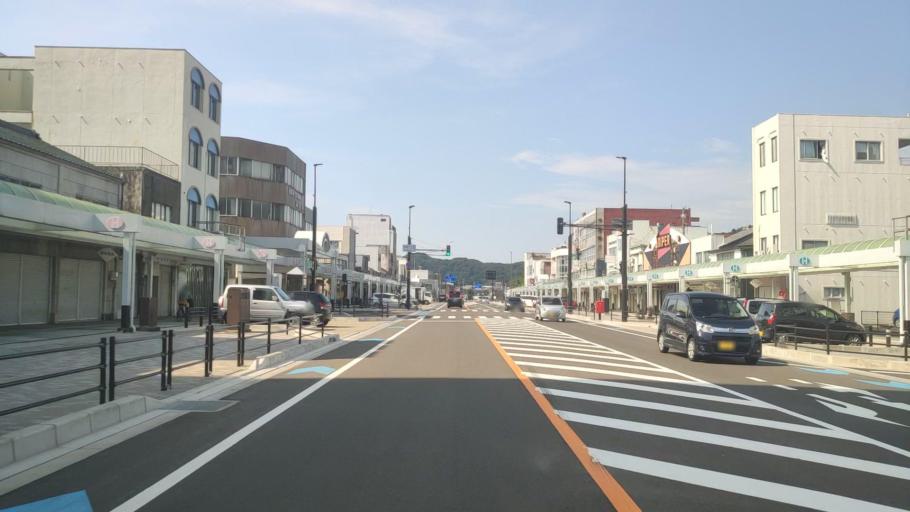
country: JP
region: Fukui
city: Tsuruga
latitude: 35.6521
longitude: 136.0729
